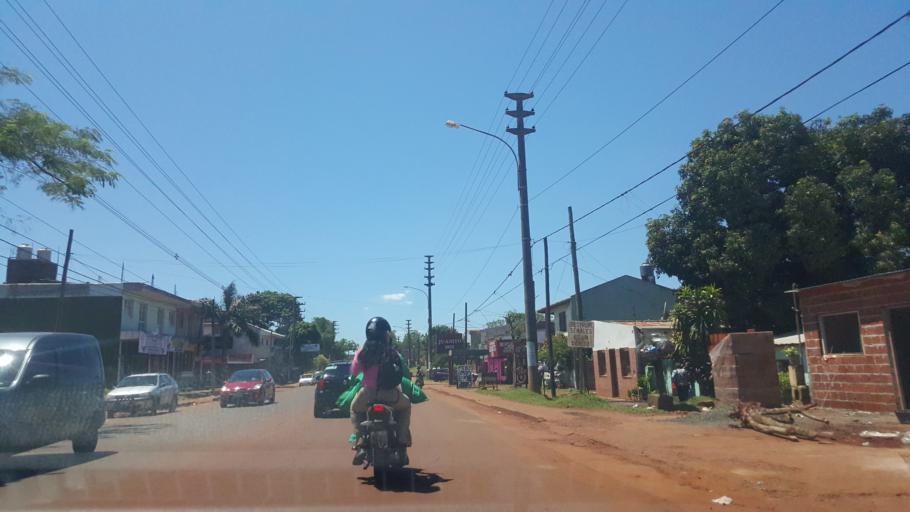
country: AR
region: Misiones
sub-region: Departamento de Capital
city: Posadas
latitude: -27.4112
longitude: -55.9120
